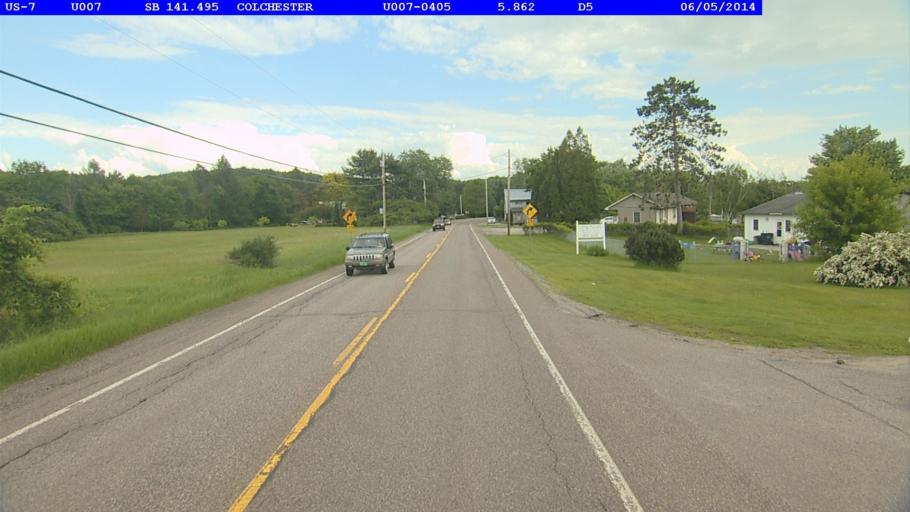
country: US
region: Vermont
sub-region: Chittenden County
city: Colchester
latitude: 44.5811
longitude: -73.1618
